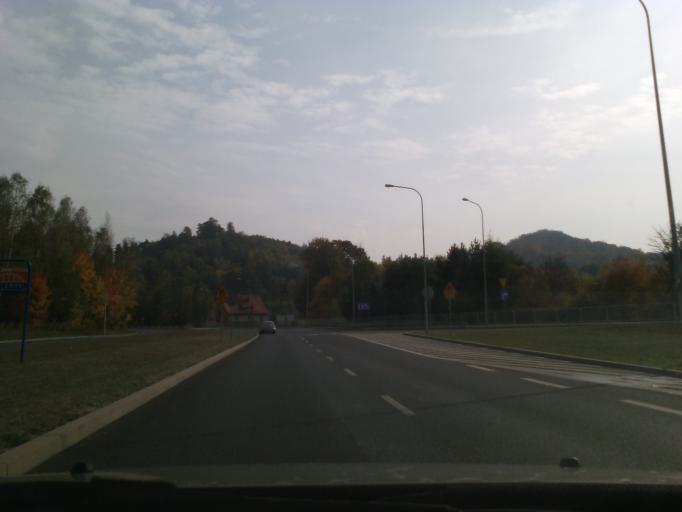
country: PL
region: Lower Silesian Voivodeship
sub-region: Powiat jeleniogorski
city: Jezow Sudecki
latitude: 50.9071
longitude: 15.7955
